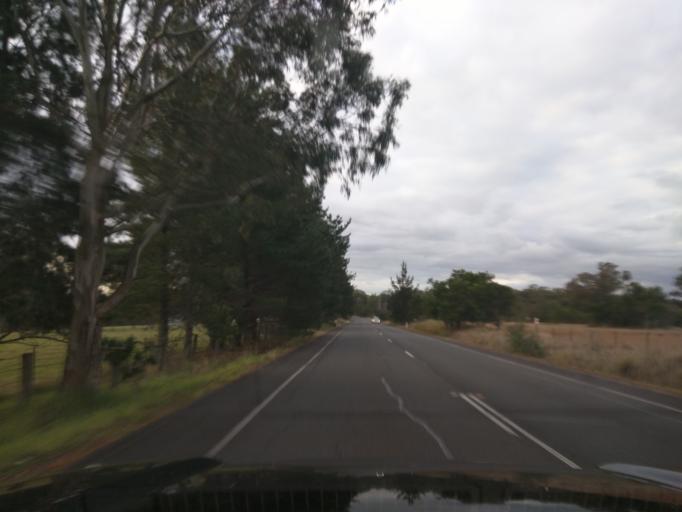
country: AU
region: New South Wales
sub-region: Wollondilly
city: Douglas Park
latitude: -34.2562
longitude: 150.7224
